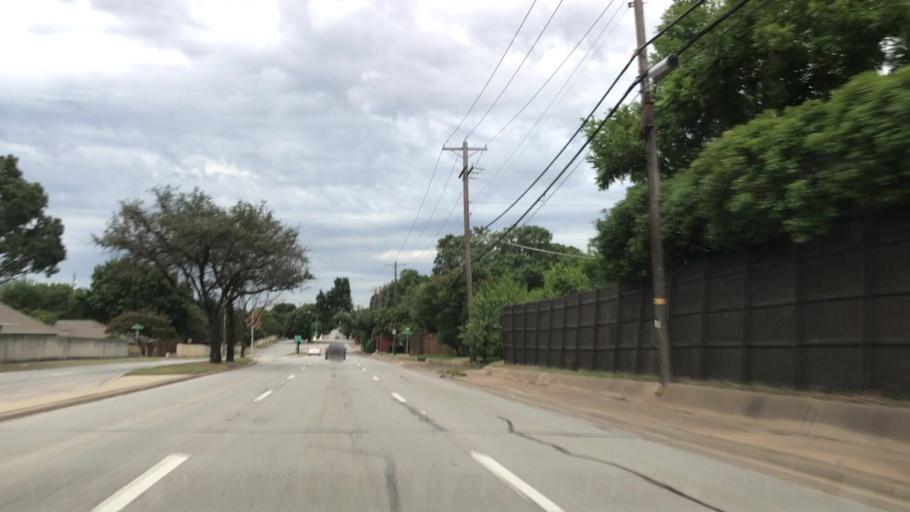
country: US
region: Texas
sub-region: Dallas County
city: University Park
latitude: 32.8913
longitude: -96.7869
